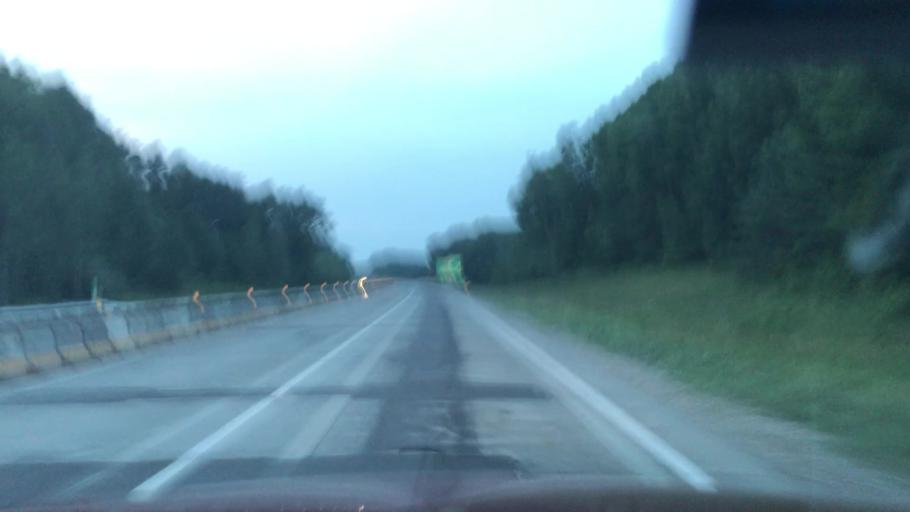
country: US
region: Michigan
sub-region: Kent County
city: Rockford
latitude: 43.1658
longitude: -85.5754
